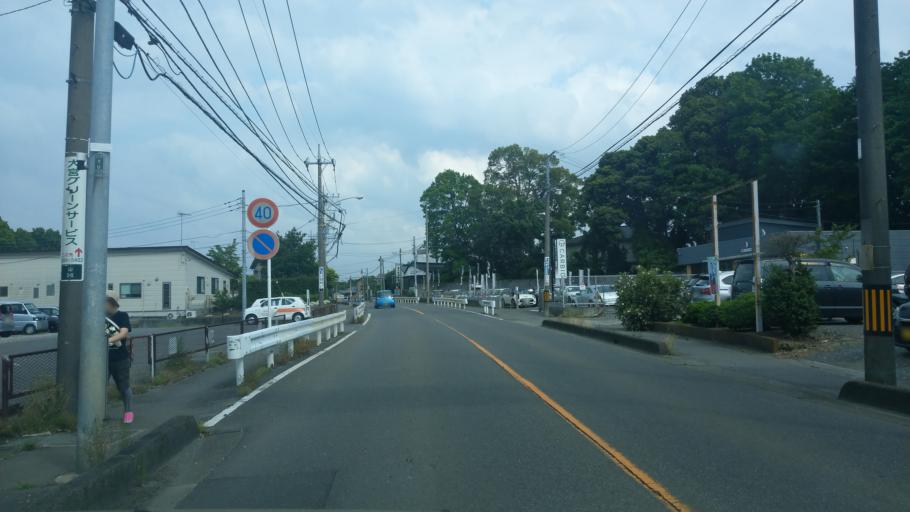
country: JP
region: Saitama
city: Saitama
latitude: 35.9053
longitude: 139.6780
